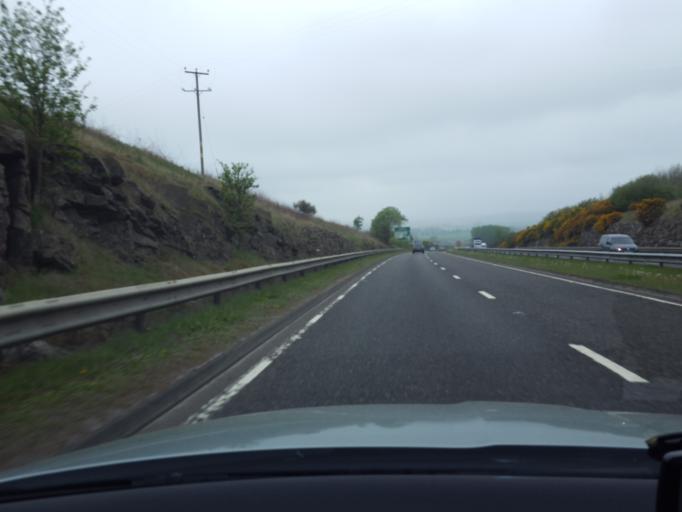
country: GB
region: Scotland
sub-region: Angus
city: Forfar
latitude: 56.6240
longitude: -2.9121
